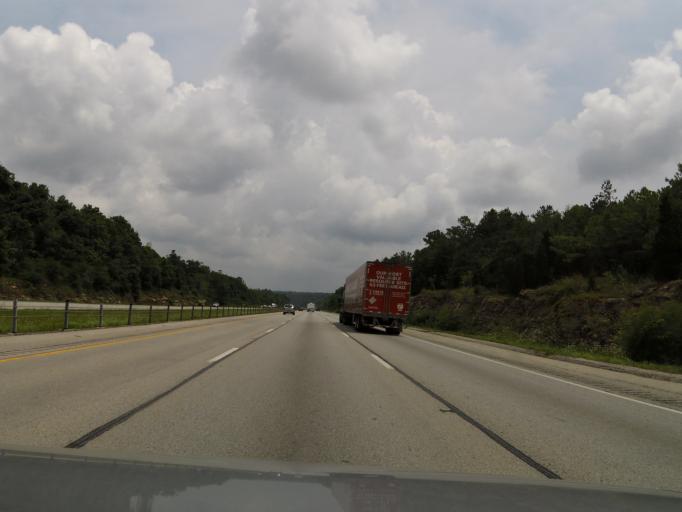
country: US
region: Kentucky
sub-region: Hardin County
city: Elizabethtown
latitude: 37.7321
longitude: -85.8132
